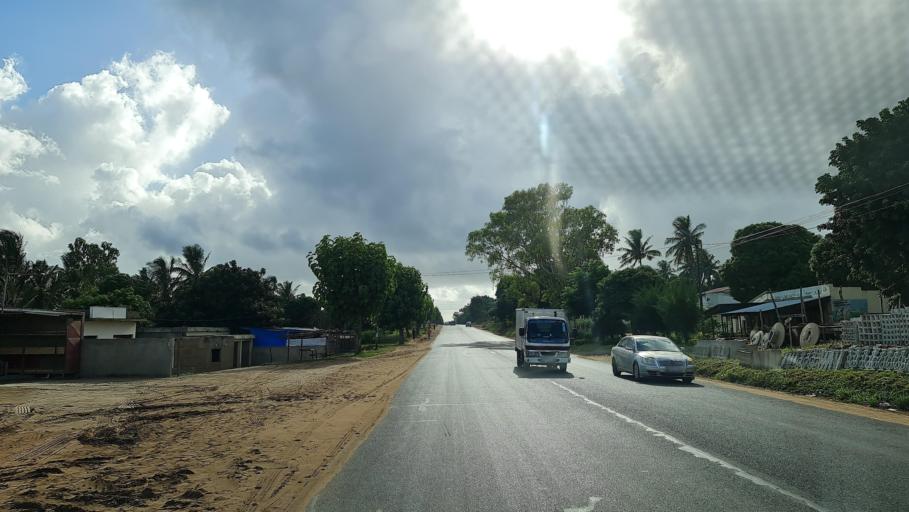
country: MZ
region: Gaza
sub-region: Xai-Xai District
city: Xai-Xai
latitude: -25.0562
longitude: 33.6868
